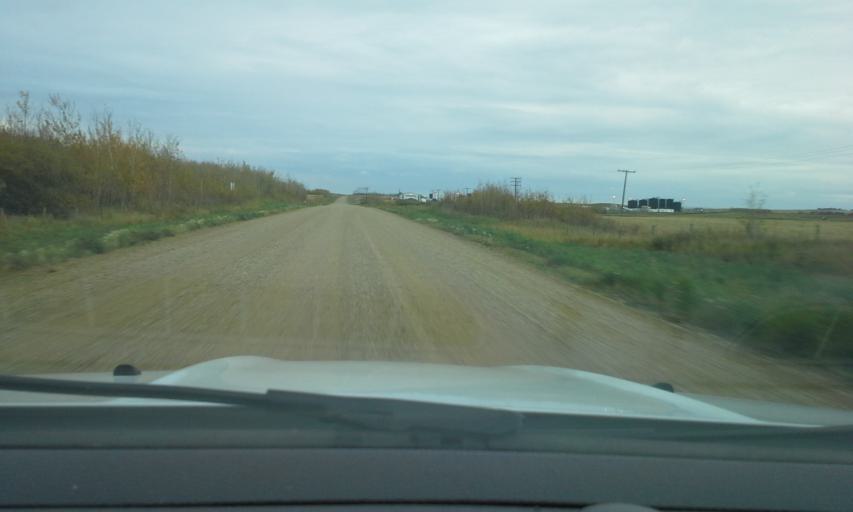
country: CA
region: Saskatchewan
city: Lloydminster
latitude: 53.2885
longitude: -109.8084
